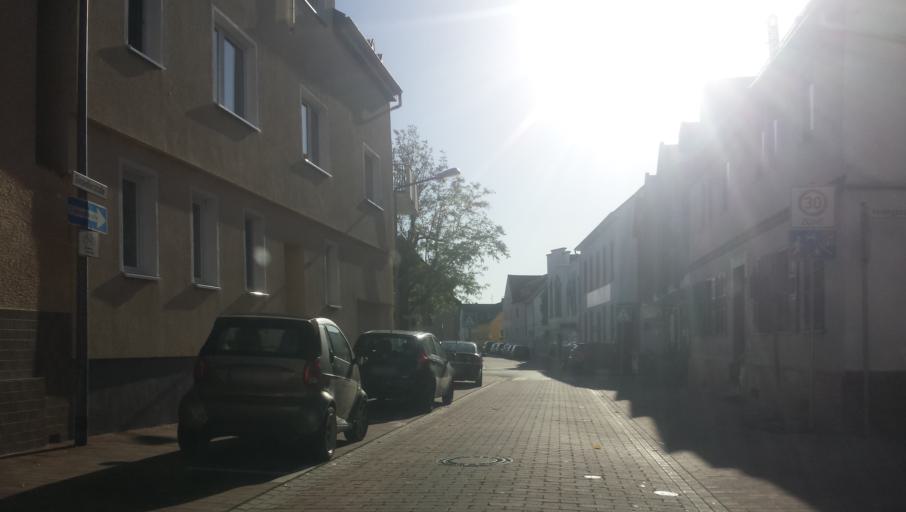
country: DE
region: Hesse
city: Gernsheim
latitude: 49.7509
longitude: 8.4857
